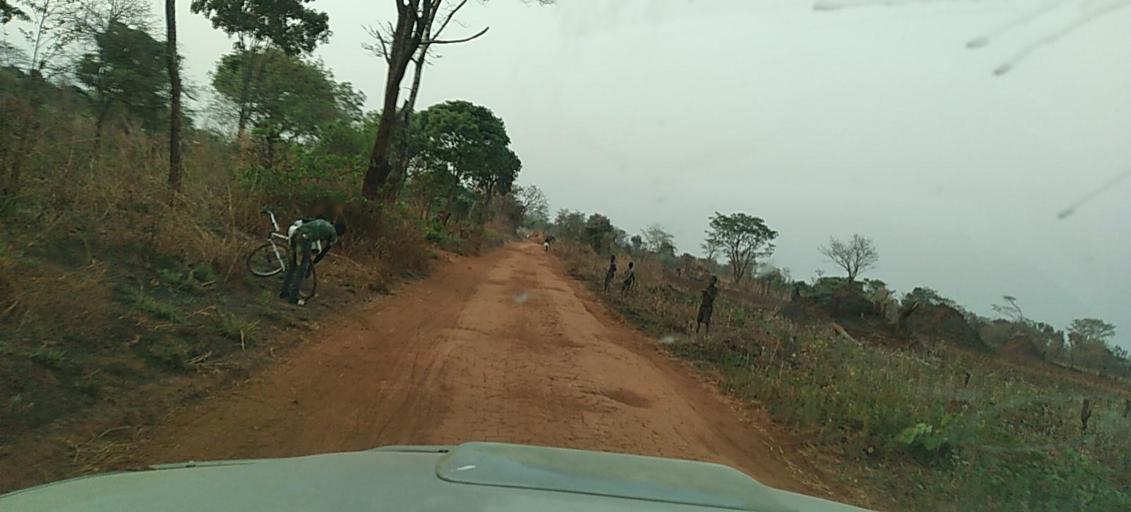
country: ZM
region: North-Western
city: Kasempa
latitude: -13.0637
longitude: 26.3818
